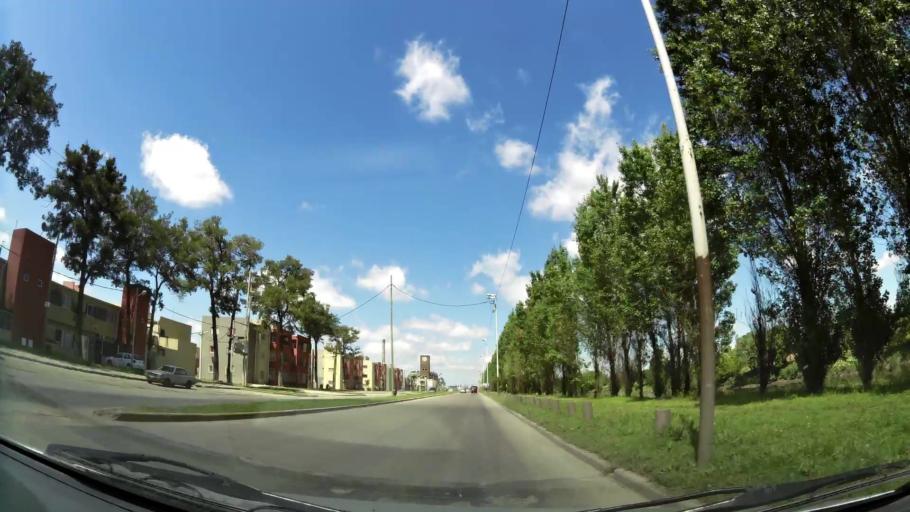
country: AR
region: Buenos Aires F.D.
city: Villa Lugano
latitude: -34.6765
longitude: -58.4361
